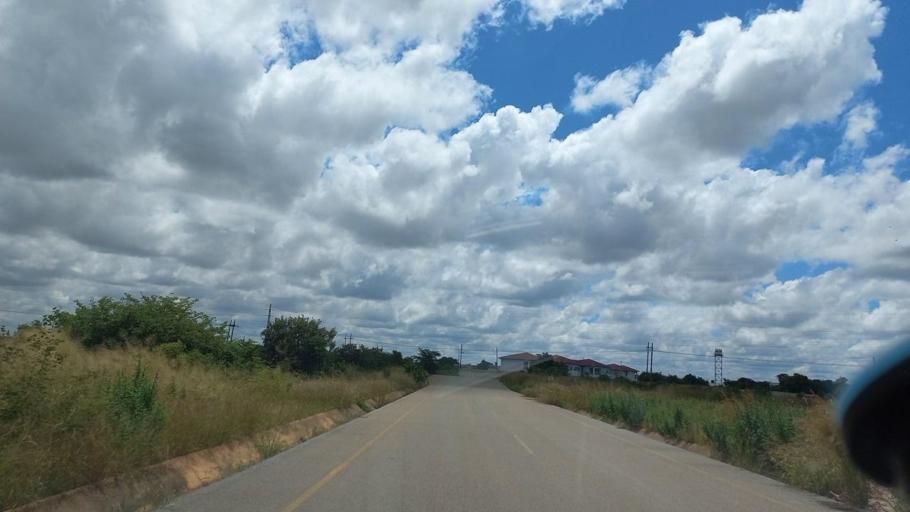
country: ZM
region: Lusaka
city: Lusaka
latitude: -15.4918
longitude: 28.3725
